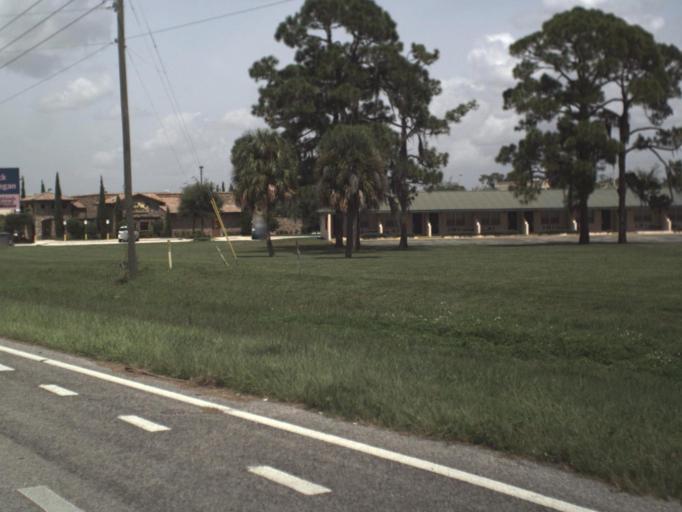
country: US
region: Florida
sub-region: Highlands County
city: Sebring
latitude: 27.4960
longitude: -81.4871
